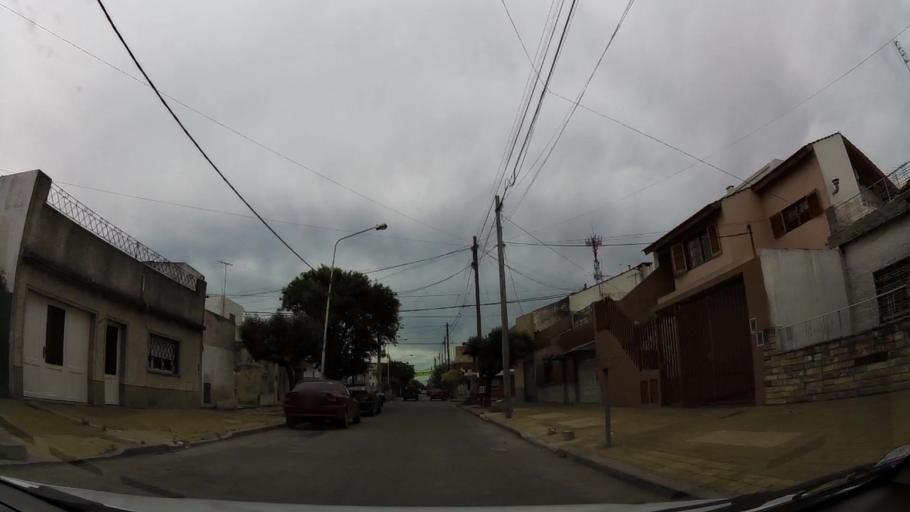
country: AR
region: Buenos Aires F.D.
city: Villa Lugano
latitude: -34.6777
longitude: -58.5096
